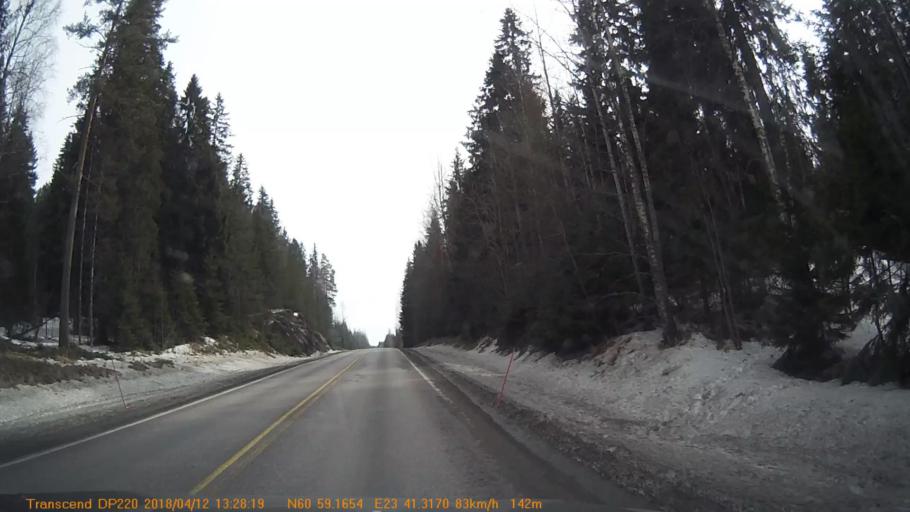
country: FI
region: Pirkanmaa
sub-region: Etelae-Pirkanmaa
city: Kylmaekoski
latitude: 60.9858
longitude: 23.6888
